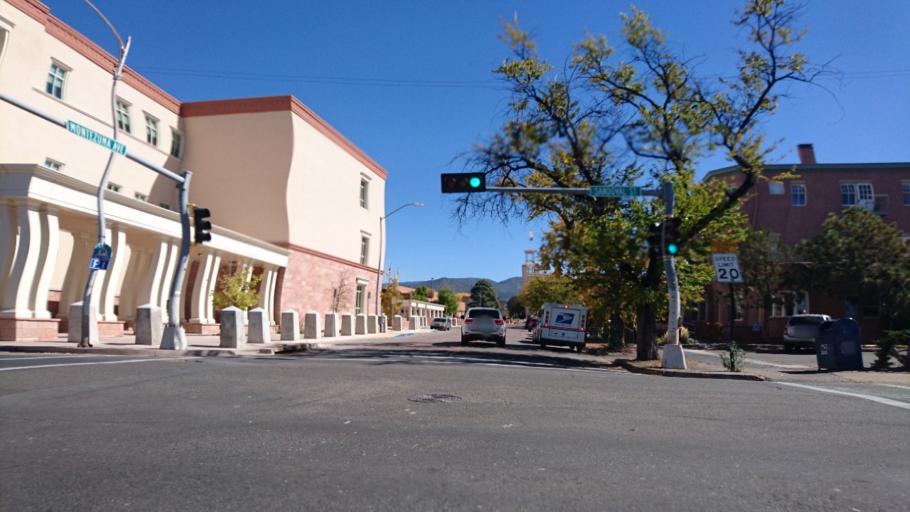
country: US
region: New Mexico
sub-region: Santa Fe County
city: Santa Fe
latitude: 35.6847
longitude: -105.9443
